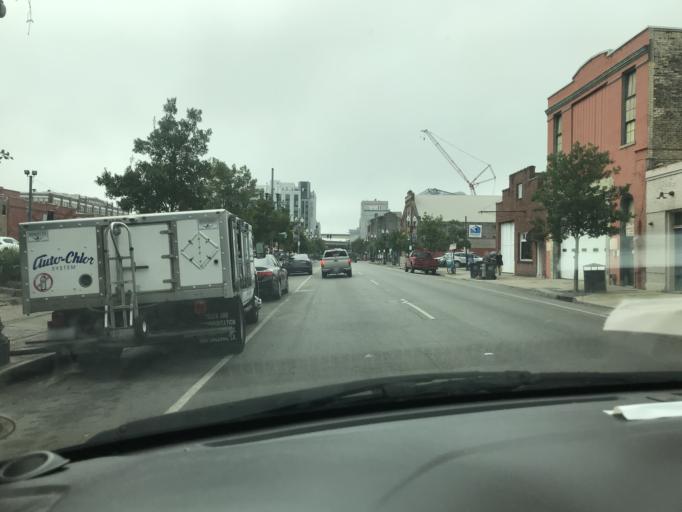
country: US
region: Louisiana
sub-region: Orleans Parish
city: New Orleans
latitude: 29.9451
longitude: -90.0693
